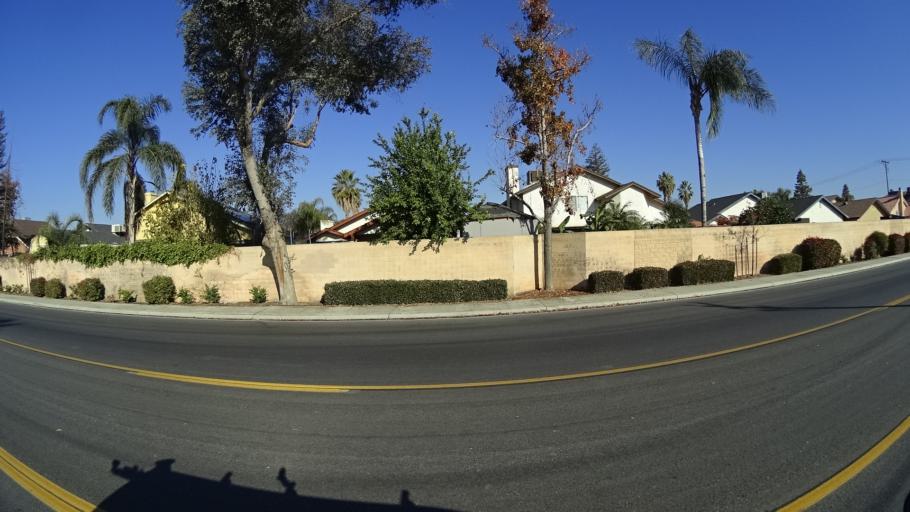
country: US
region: California
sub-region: Kern County
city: Greenfield
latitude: 35.3104
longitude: -119.0266
